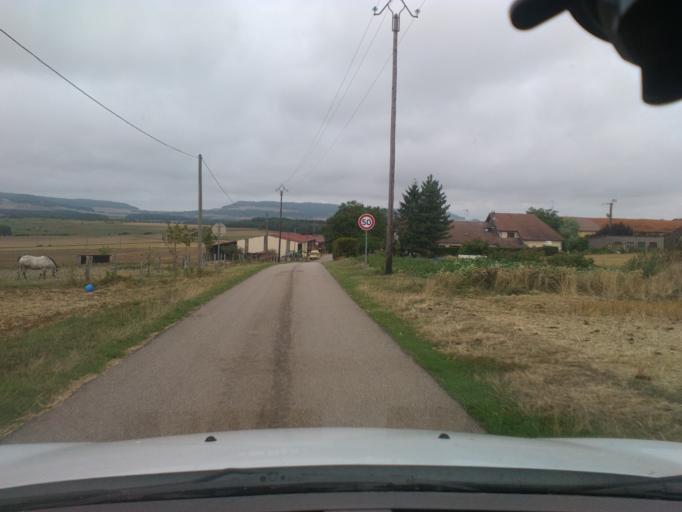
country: FR
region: Lorraine
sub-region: Departement des Vosges
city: Mirecourt
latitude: 48.3617
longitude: 6.1274
